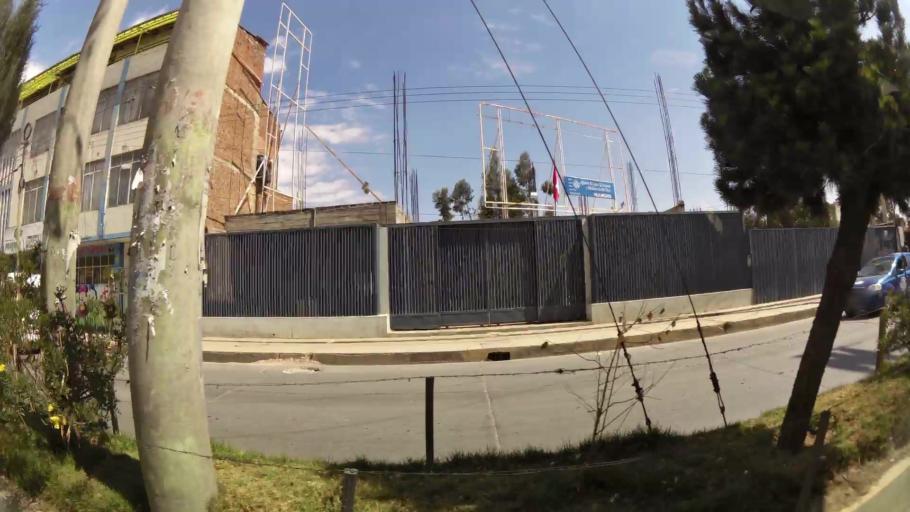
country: PE
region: Junin
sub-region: Provincia de Huancayo
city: El Tambo
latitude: -12.0687
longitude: -75.2157
